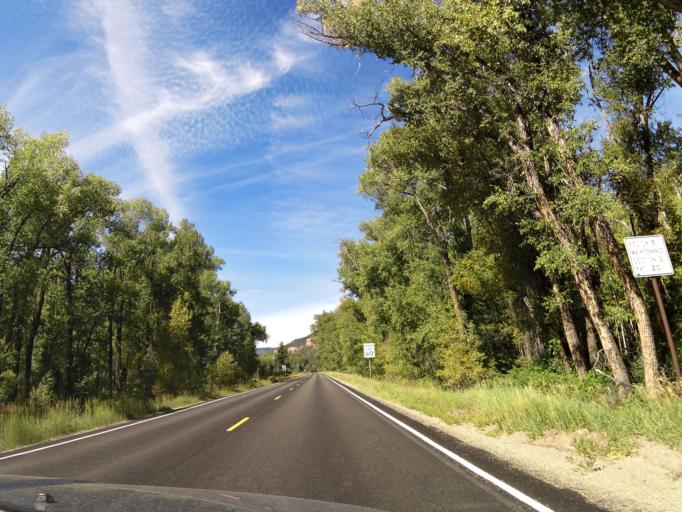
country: US
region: Colorado
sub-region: Montezuma County
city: Mancos
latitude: 37.5785
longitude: -108.2166
